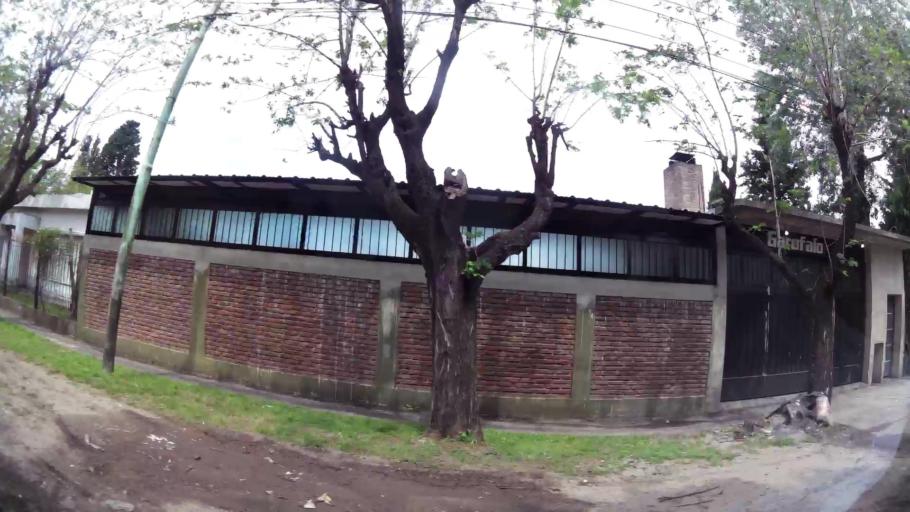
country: AR
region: Buenos Aires
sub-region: Partido de Quilmes
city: Quilmes
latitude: -34.7757
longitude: -58.2635
